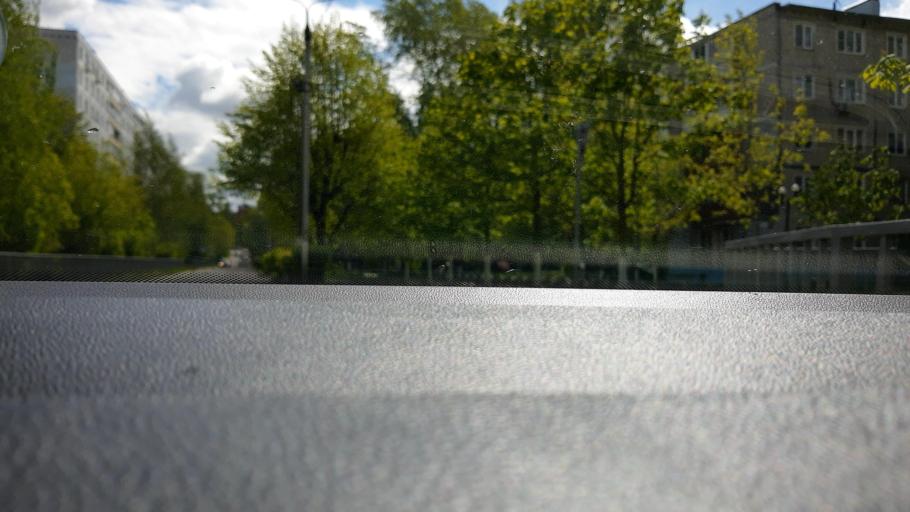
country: RU
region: Moskovskaya
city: Dmitrov
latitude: 56.3502
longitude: 37.5266
